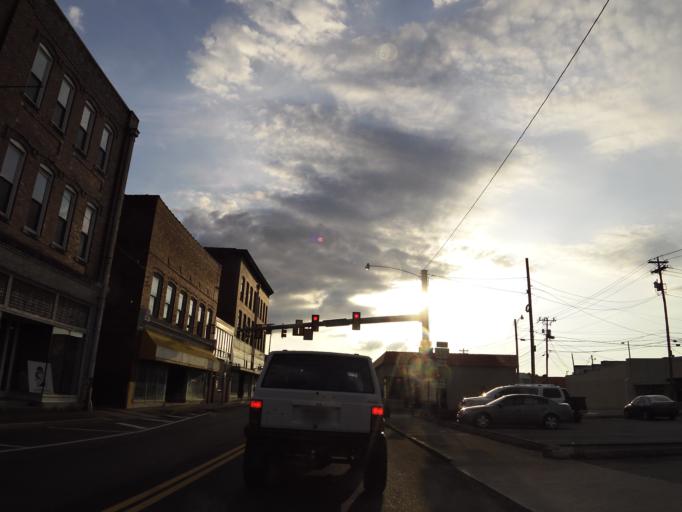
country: US
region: Tennessee
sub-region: Cocke County
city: Newport
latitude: 35.9669
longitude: -83.1870
